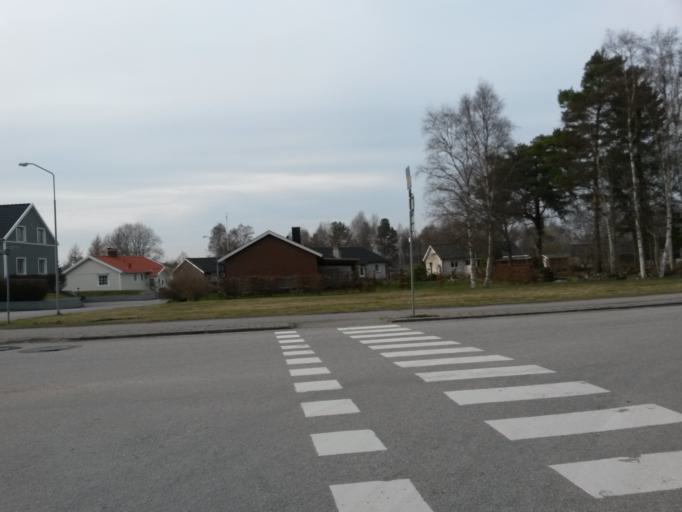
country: SE
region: Vaestra Goetaland
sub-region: Herrljunga Kommun
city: Herrljunga
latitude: 58.0707
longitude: 13.0229
